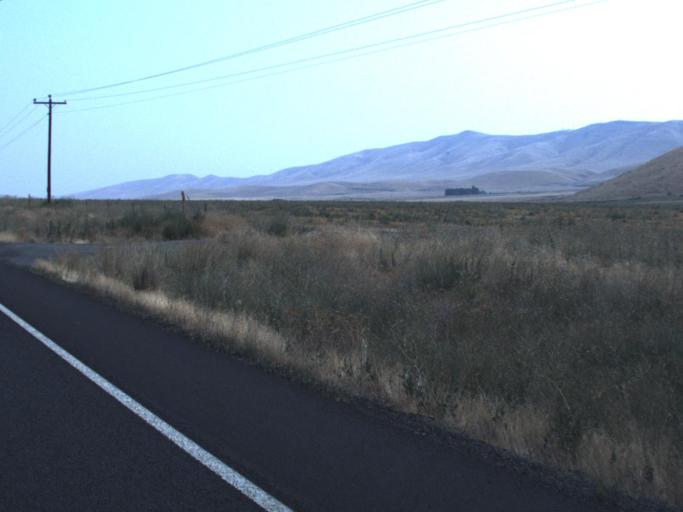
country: US
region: Washington
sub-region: Yakima County
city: Sunnyside
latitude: 46.5091
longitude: -120.0706
